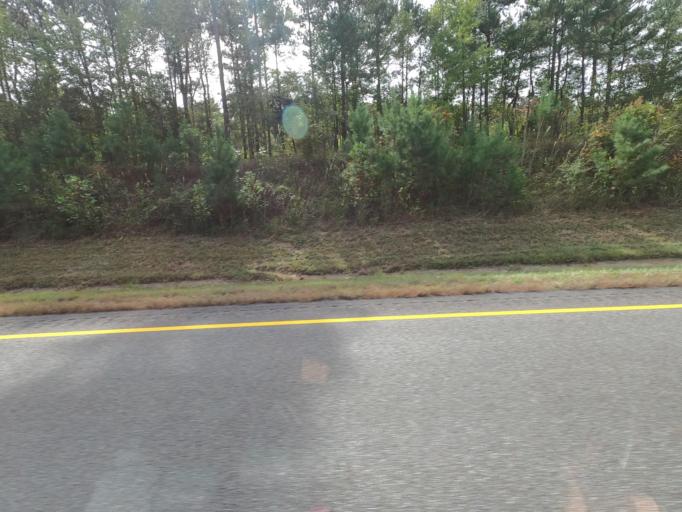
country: US
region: Tennessee
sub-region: Decatur County
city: Parsons
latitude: 35.8150
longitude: -88.2115
